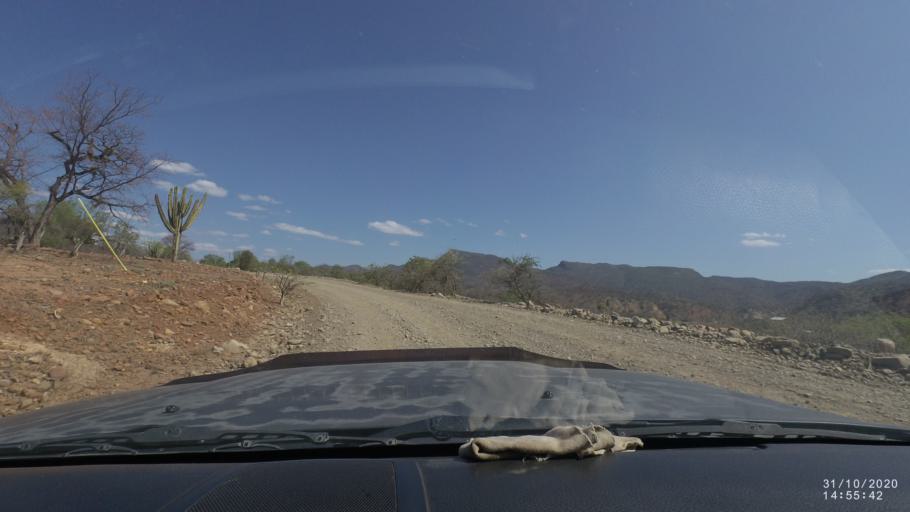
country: BO
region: Cochabamba
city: Aiquile
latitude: -18.2341
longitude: -64.8565
